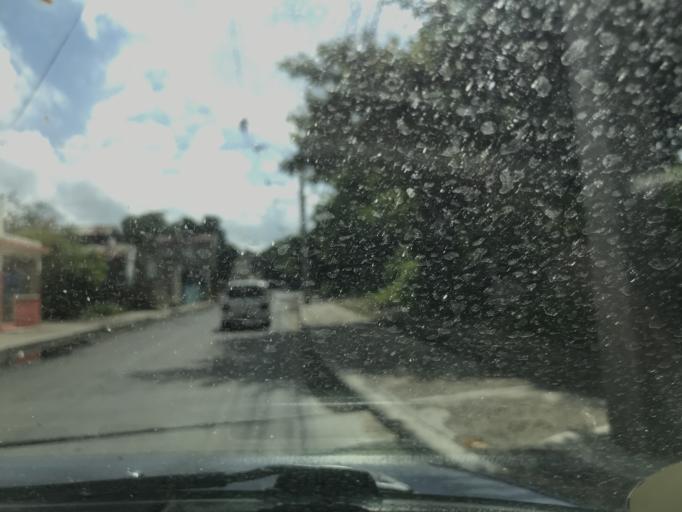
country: DO
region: Santiago
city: Santiago de los Caballeros
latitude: 19.4534
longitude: -70.7270
